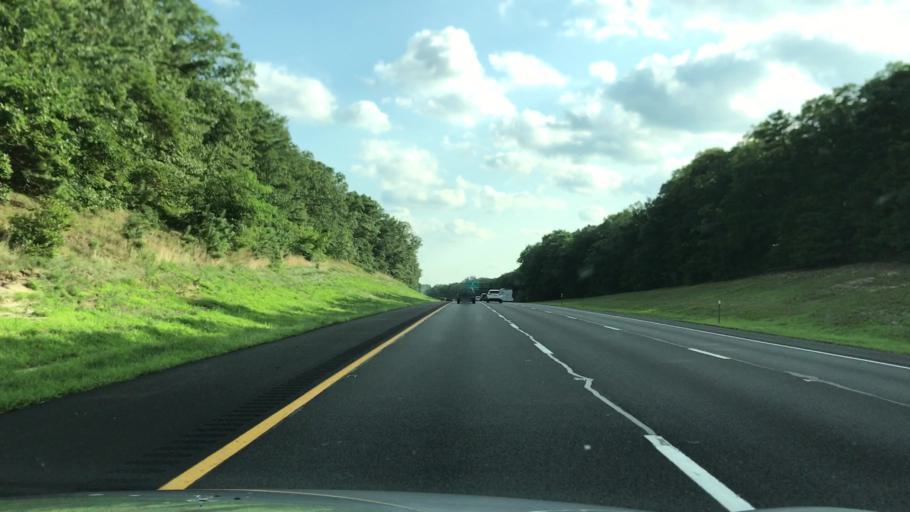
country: US
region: New Jersey
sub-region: Ocean County
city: Ocean Acres
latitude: 39.7219
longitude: -74.2718
